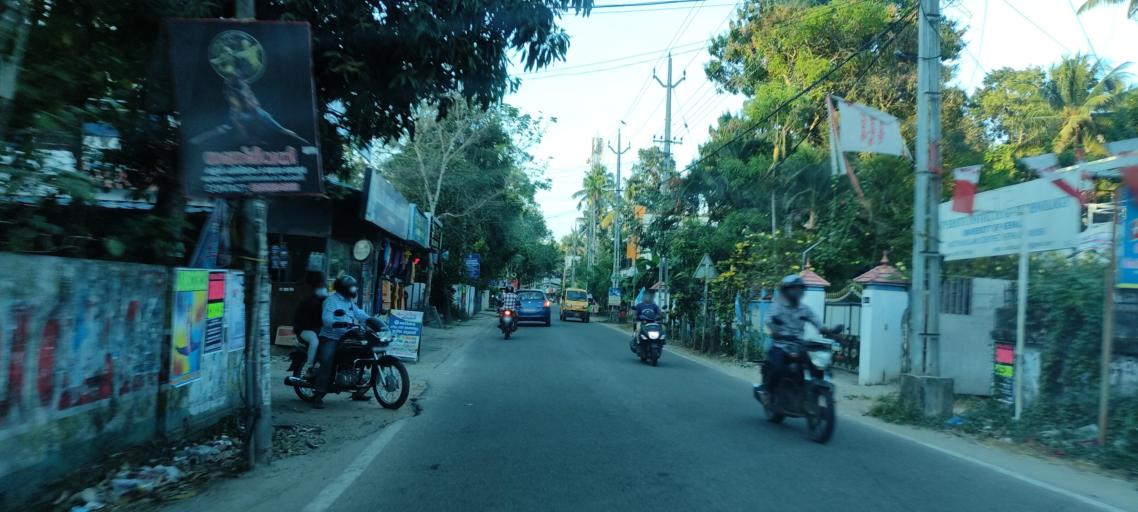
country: IN
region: Kerala
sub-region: Alappuzha
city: Kayankulam
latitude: 9.2138
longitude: 76.4616
